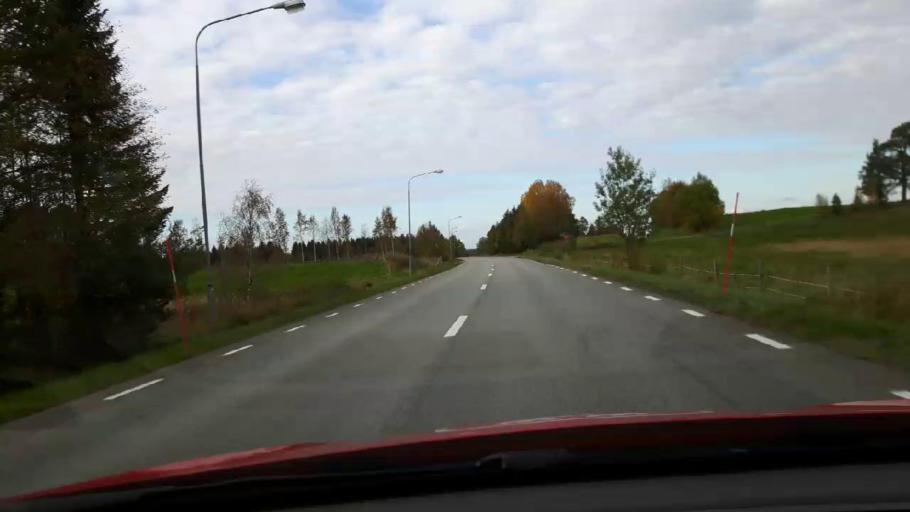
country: SE
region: Jaemtland
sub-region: Krokoms Kommun
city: Valla
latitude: 63.2364
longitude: 14.0074
